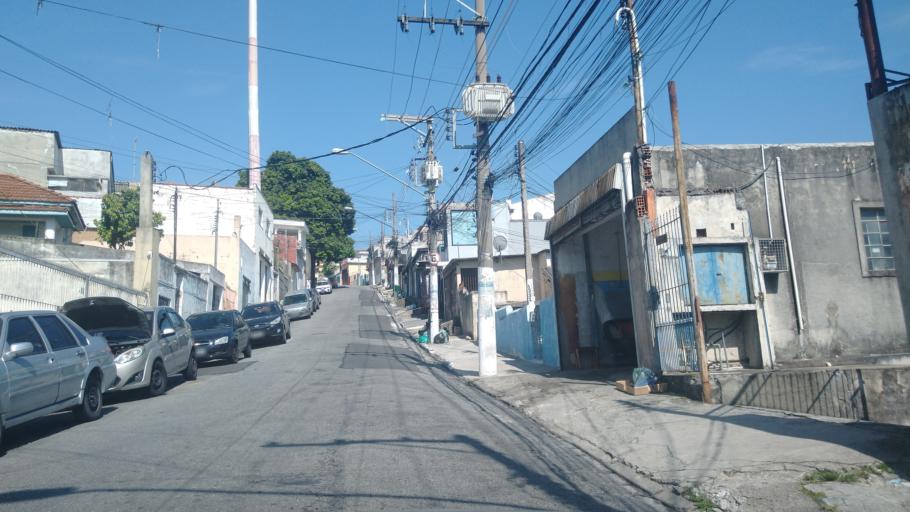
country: BR
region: Sao Paulo
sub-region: Sao Paulo
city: Sao Paulo
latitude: -23.4918
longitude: -46.6632
